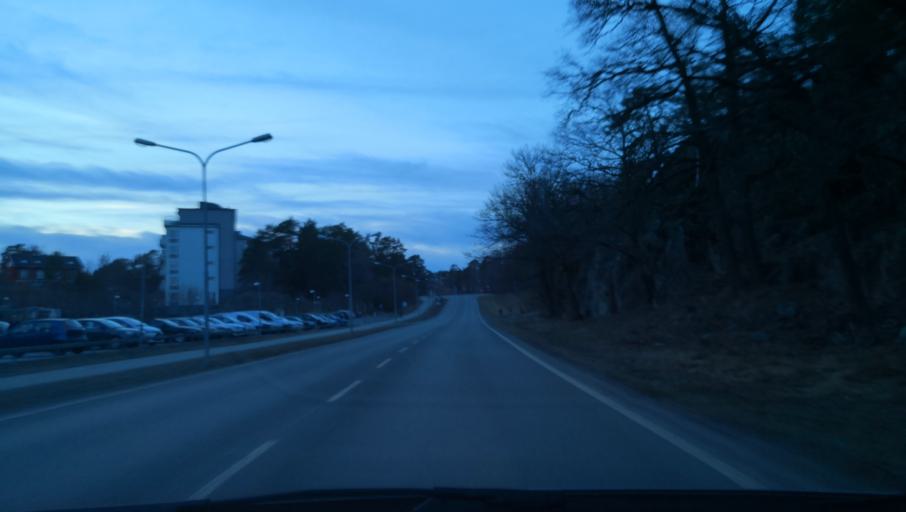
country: SE
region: Stockholm
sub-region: Varmdo Kommun
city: Gustavsberg
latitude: 59.3303
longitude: 18.3907
